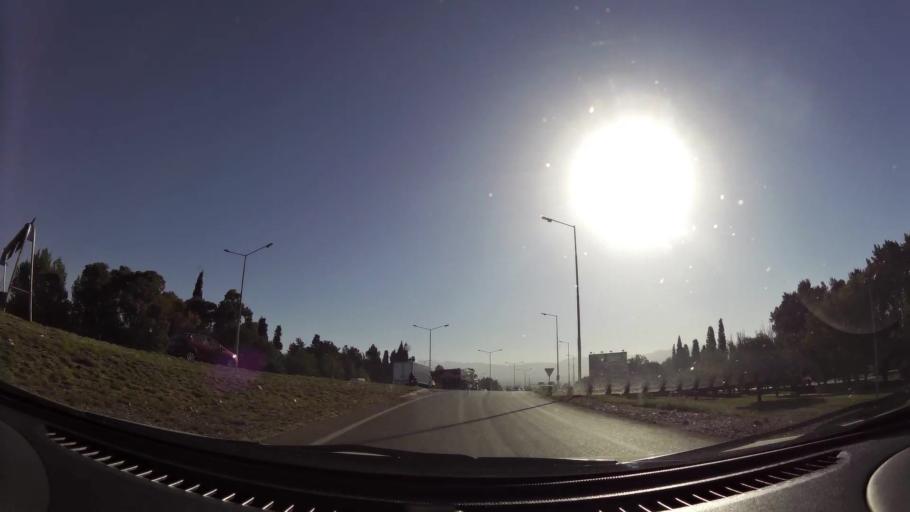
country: AR
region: Mendoza
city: Mendoza
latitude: -32.8973
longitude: -68.8123
